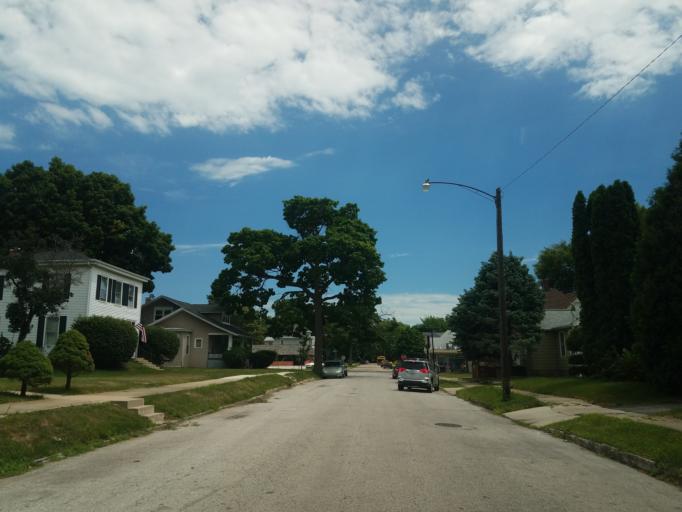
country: US
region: Illinois
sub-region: McLean County
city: Bloomington
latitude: 40.4838
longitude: -88.9858
